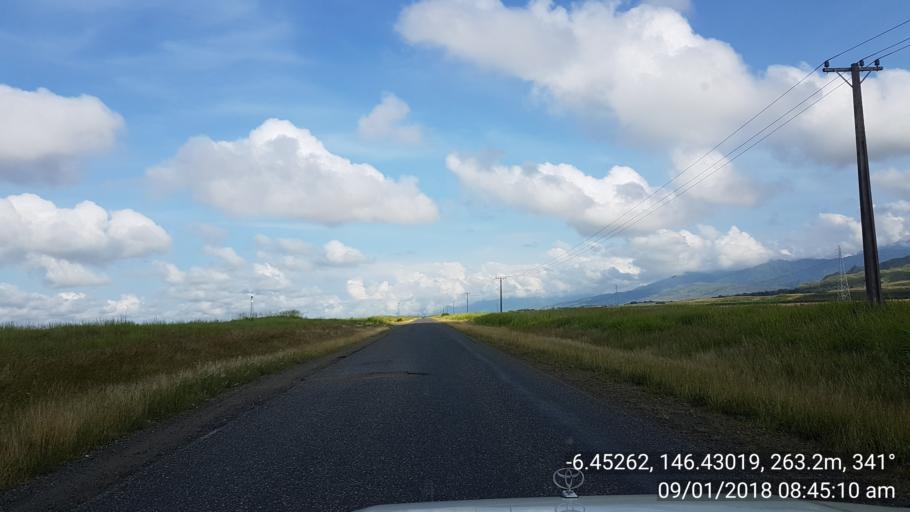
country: PG
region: Eastern Highlands
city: Kainantu
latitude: -6.4527
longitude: 146.4302
